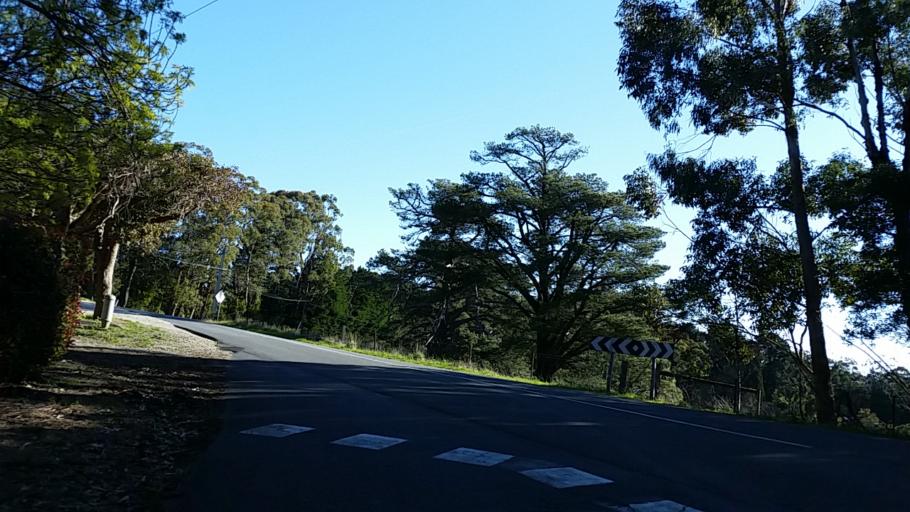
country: AU
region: South Australia
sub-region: Adelaide Hills
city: Adelaide Hills
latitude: -34.9324
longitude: 138.7450
